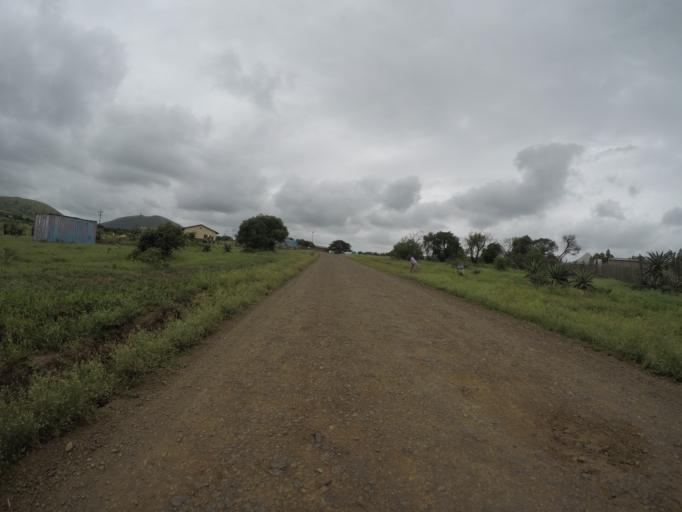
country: ZA
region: KwaZulu-Natal
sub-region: uThungulu District Municipality
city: Empangeni
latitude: -28.6098
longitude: 31.8648
